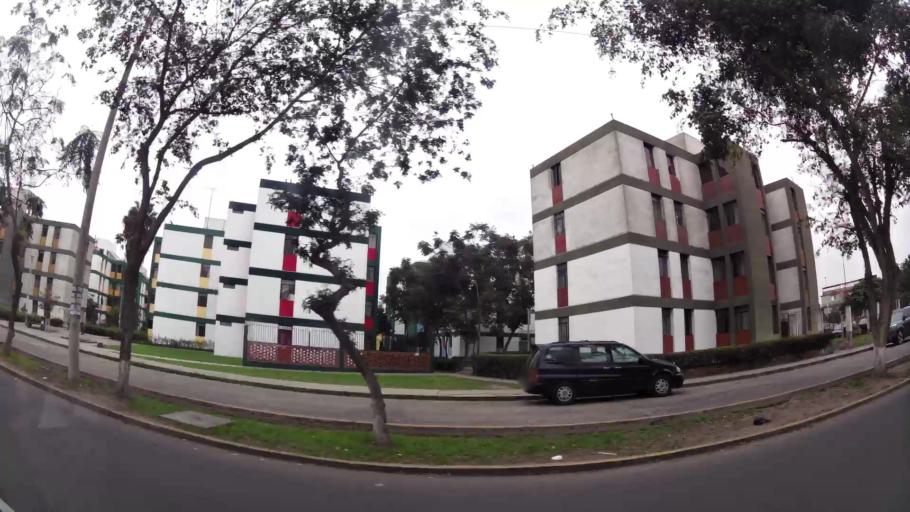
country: PE
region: Lima
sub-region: Lima
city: San Luis
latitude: -12.0800
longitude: -77.0078
